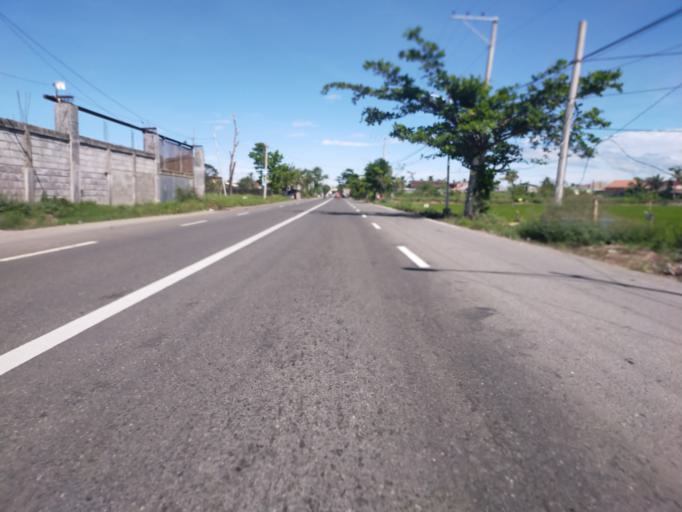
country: PH
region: Central Luzon
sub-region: Province of Bulacan
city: Bulualto
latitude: 15.2343
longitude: 120.9549
